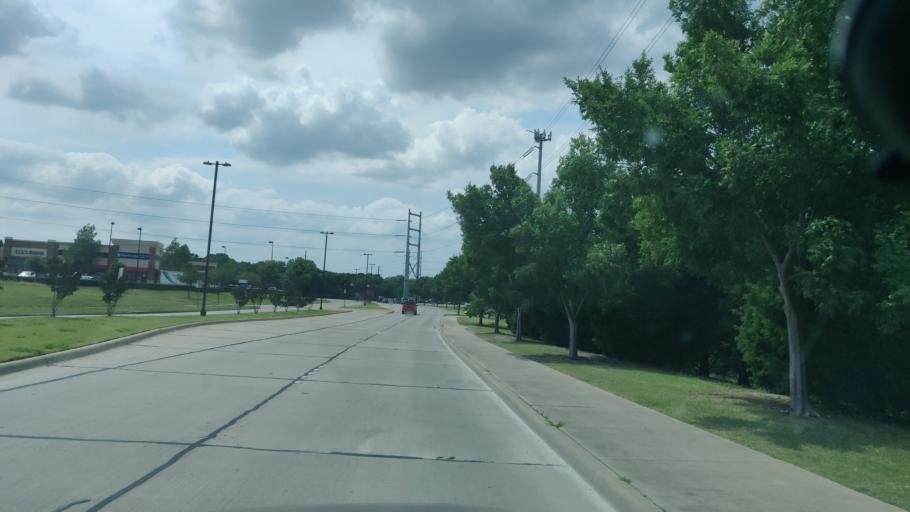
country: US
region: Texas
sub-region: Dallas County
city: Sachse
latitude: 32.9570
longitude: -96.6135
